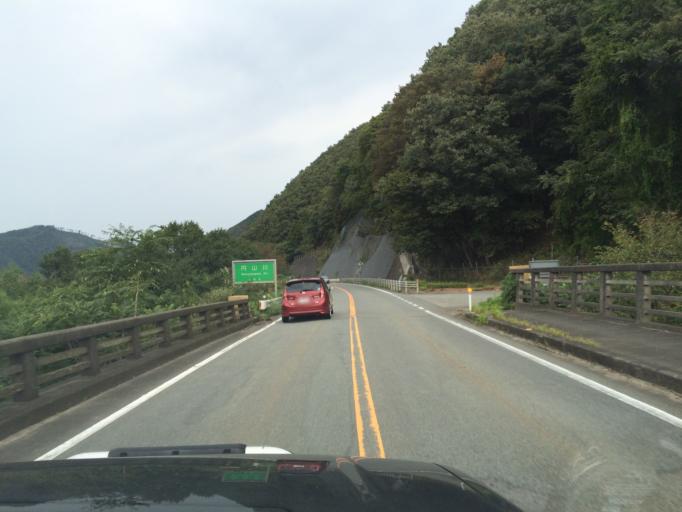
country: JP
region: Hyogo
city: Toyooka
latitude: 35.3612
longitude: 134.8281
